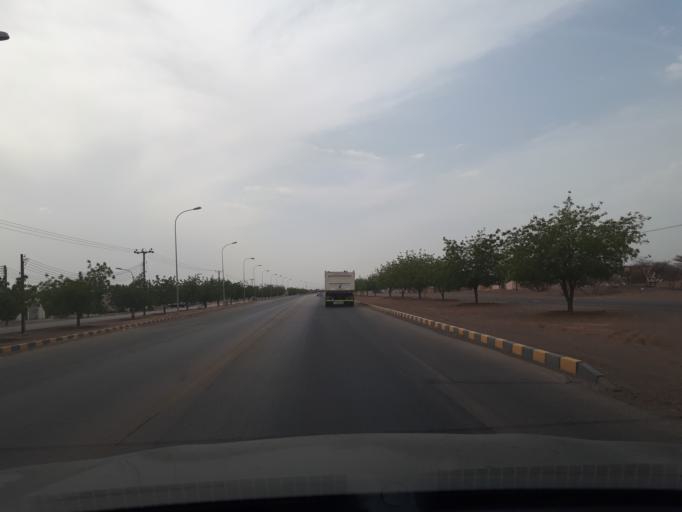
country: OM
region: Ash Sharqiyah
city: Badiyah
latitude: 22.4600
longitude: 58.7997
